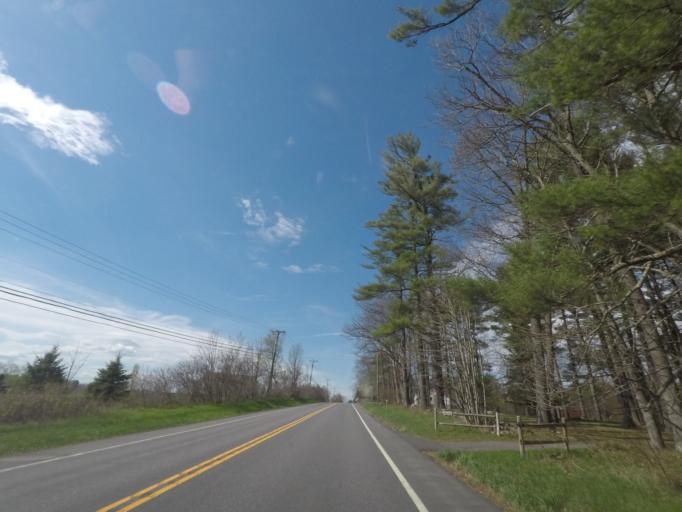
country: US
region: New York
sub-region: Greene County
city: Cairo
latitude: 42.3252
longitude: -74.0141
